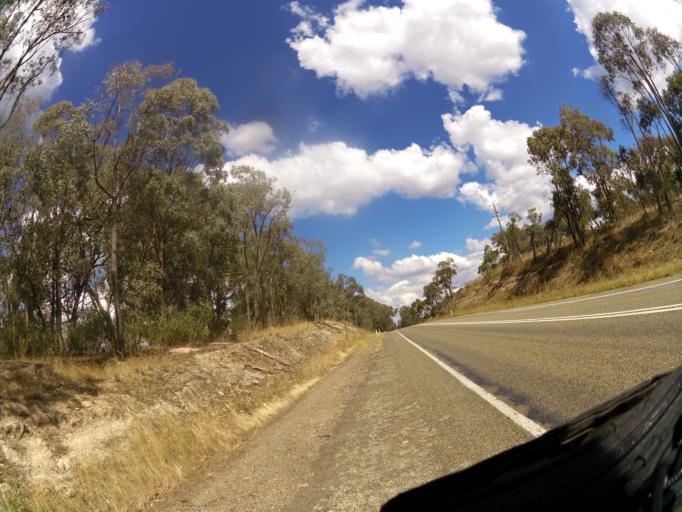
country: AU
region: Victoria
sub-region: Benalla
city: Benalla
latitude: -36.7918
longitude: 146.0108
